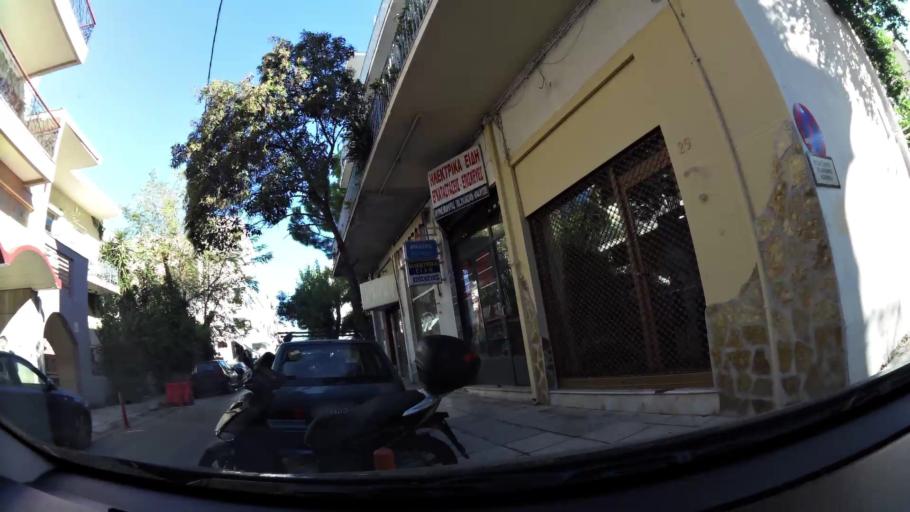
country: GR
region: Attica
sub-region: Nomarchia Athinas
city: Khalandrion
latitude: 38.0200
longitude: 23.8009
